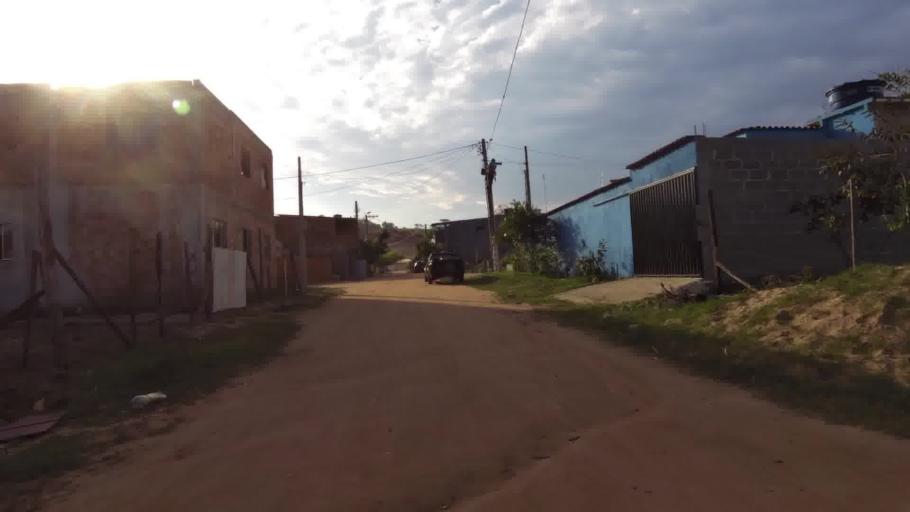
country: BR
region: Espirito Santo
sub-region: Piuma
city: Piuma
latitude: -20.8395
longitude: -40.7443
